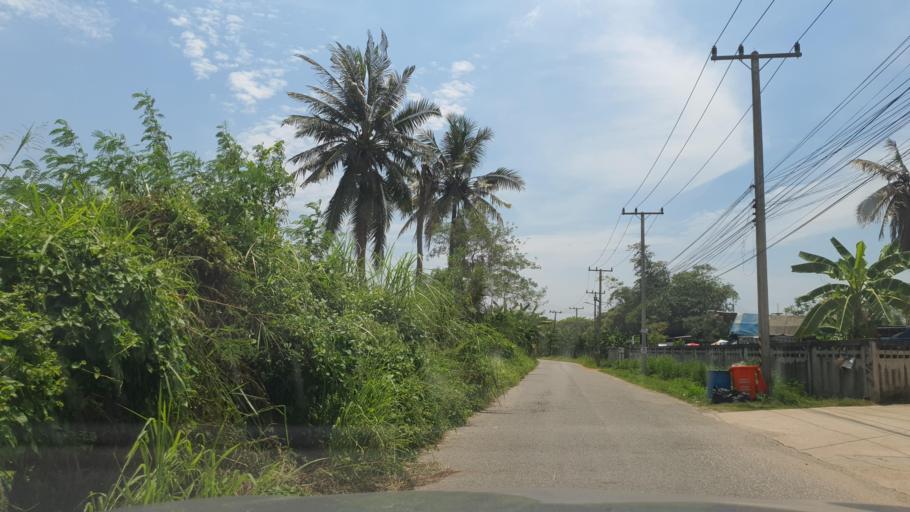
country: TH
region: Rayong
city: Ban Chang
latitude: 12.8021
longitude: 100.9492
